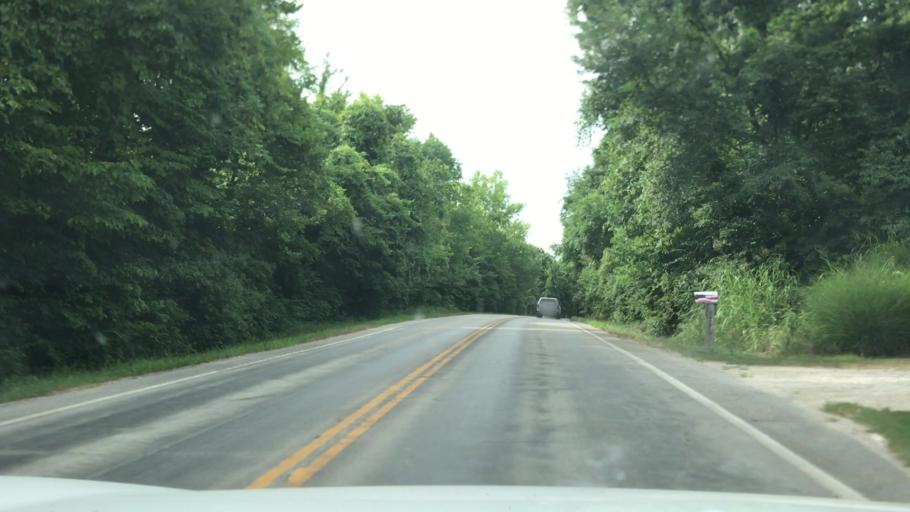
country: US
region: Missouri
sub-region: Saint Charles County
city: Weldon Spring
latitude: 38.6426
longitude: -90.7738
